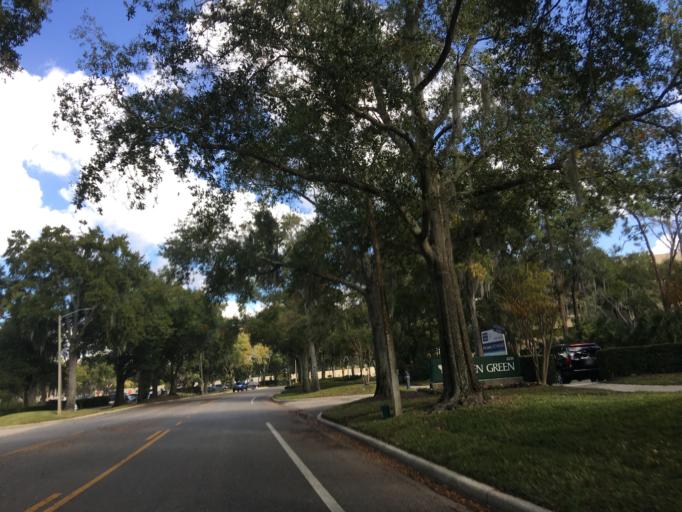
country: US
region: Florida
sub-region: Orange County
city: Eatonville
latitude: 28.6246
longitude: -81.3893
